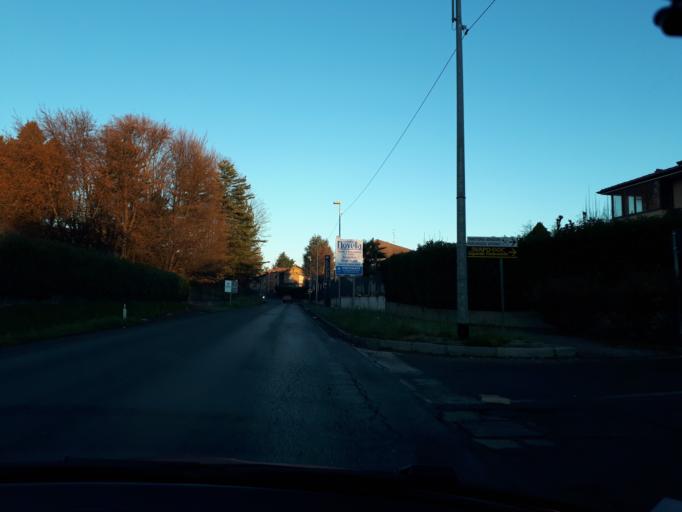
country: IT
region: Lombardy
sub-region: Provincia di Como
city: Cermenate
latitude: 45.7006
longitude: 9.0947
